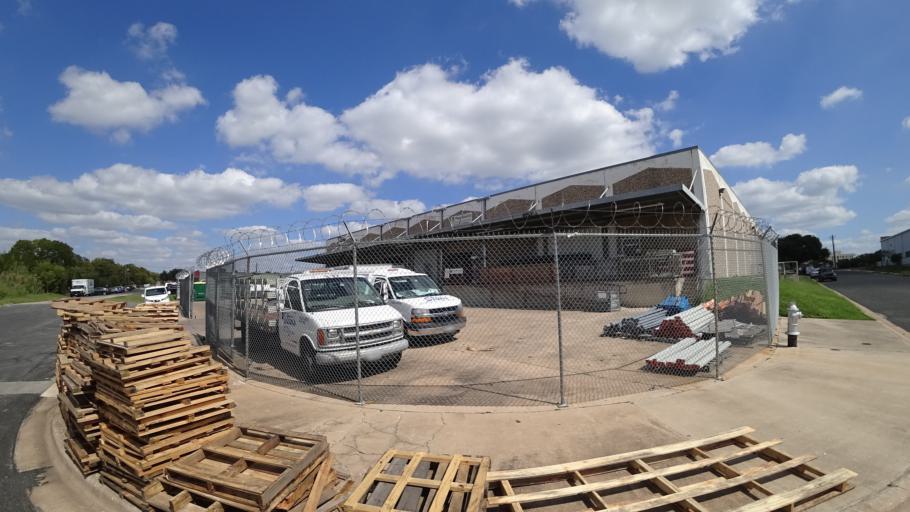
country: US
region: Texas
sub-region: Travis County
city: Austin
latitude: 30.3262
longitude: -97.7188
